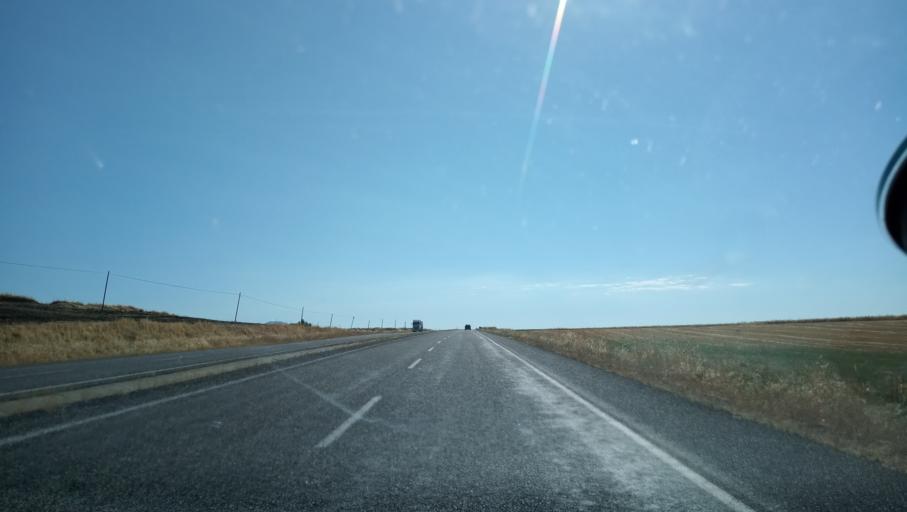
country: TR
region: Diyarbakir
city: Bagdere
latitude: 38.1297
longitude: 40.7923
